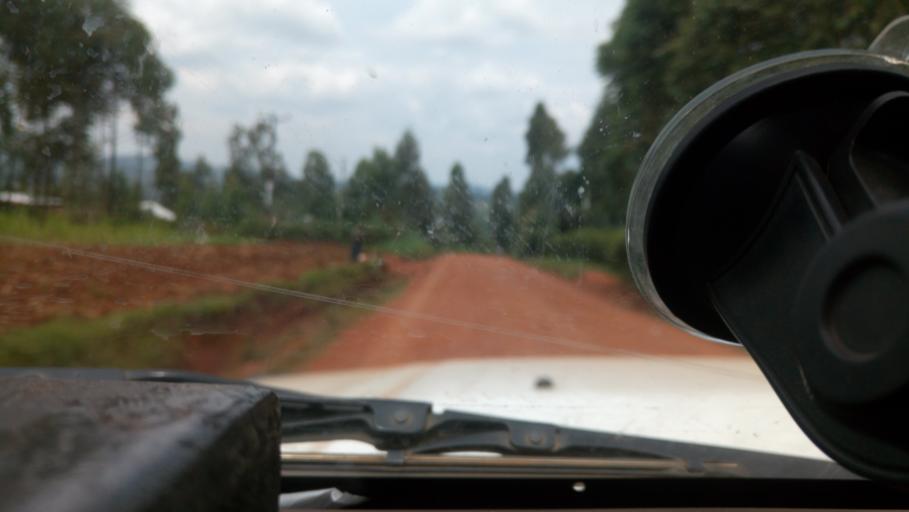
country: KE
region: Nyamira District
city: Keroka
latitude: -0.7631
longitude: 34.8885
